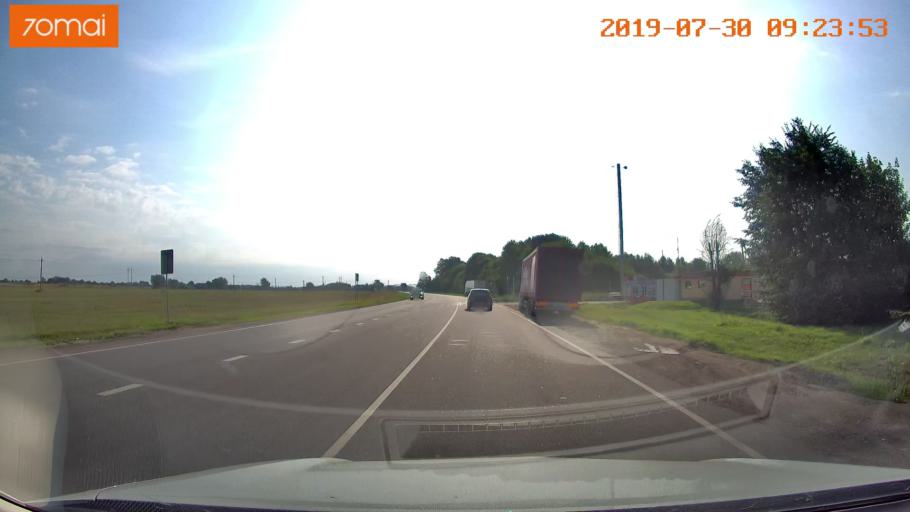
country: LT
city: Kybartai
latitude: 54.6329
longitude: 22.6829
